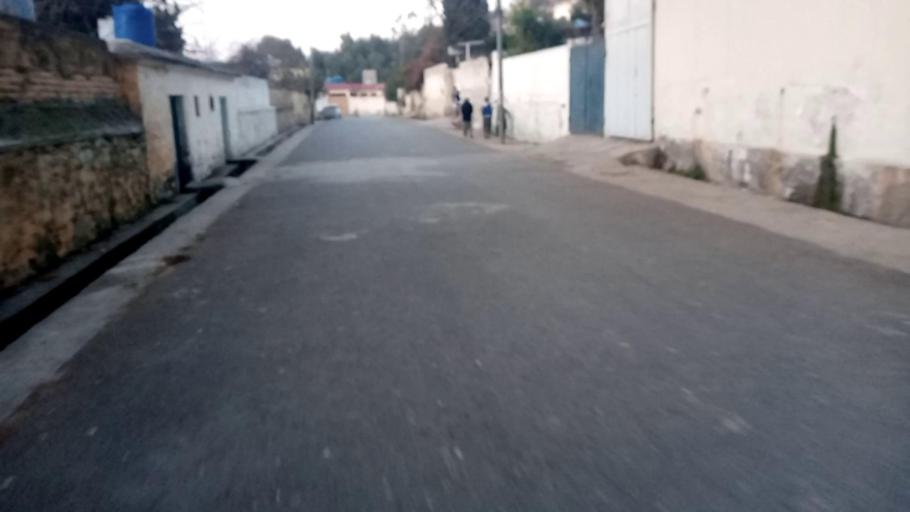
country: PK
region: Khyber Pakhtunkhwa
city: Saidu Sharif
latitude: 34.7556
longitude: 72.3610
